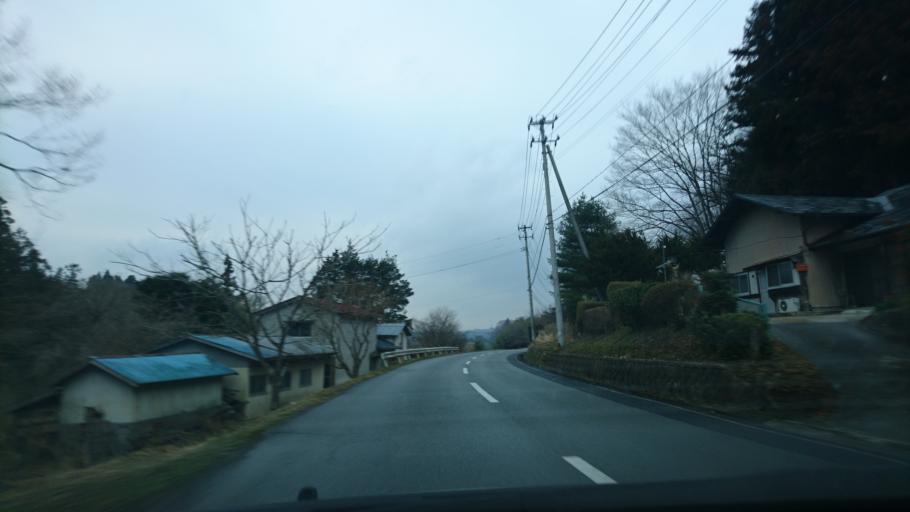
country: JP
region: Iwate
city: Ichinoseki
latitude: 39.0172
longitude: 141.3608
